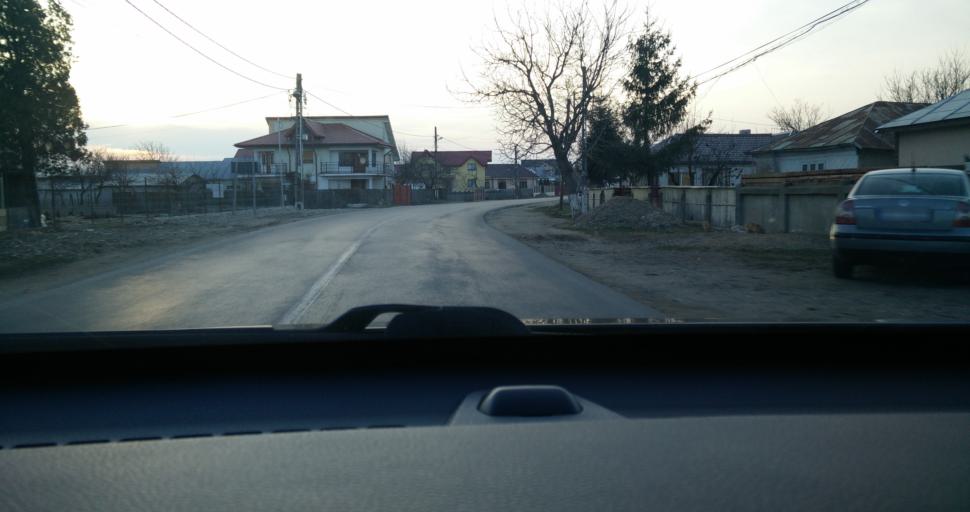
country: RO
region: Vrancea
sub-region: Comuna Rastoaca
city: Rastoaca
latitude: 45.6628
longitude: 27.2790
